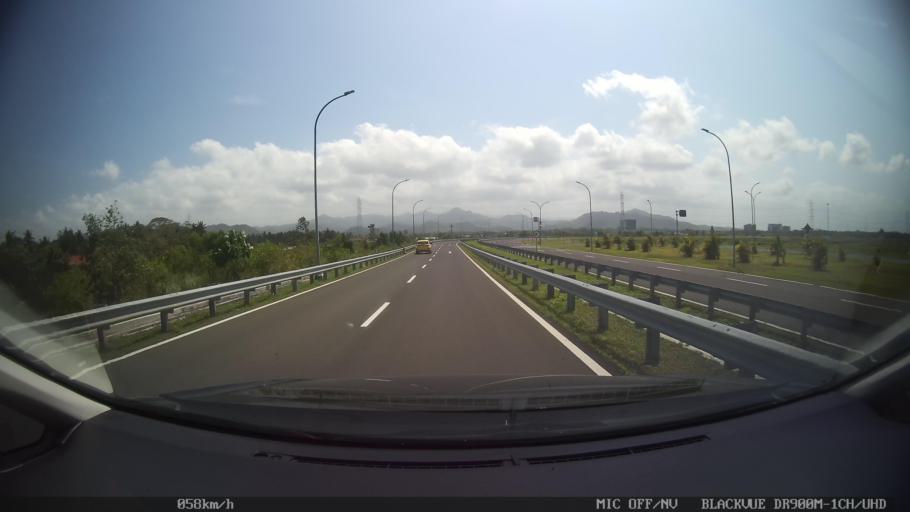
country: ID
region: Daerah Istimewa Yogyakarta
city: Srandakan
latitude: -7.8943
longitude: 110.0587
